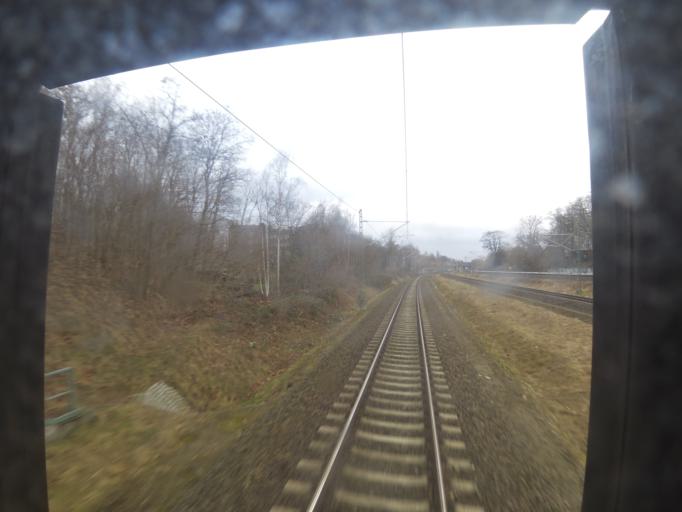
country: DE
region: Berlin
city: Schoneberg Bezirk
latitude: 52.4531
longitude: 13.3573
